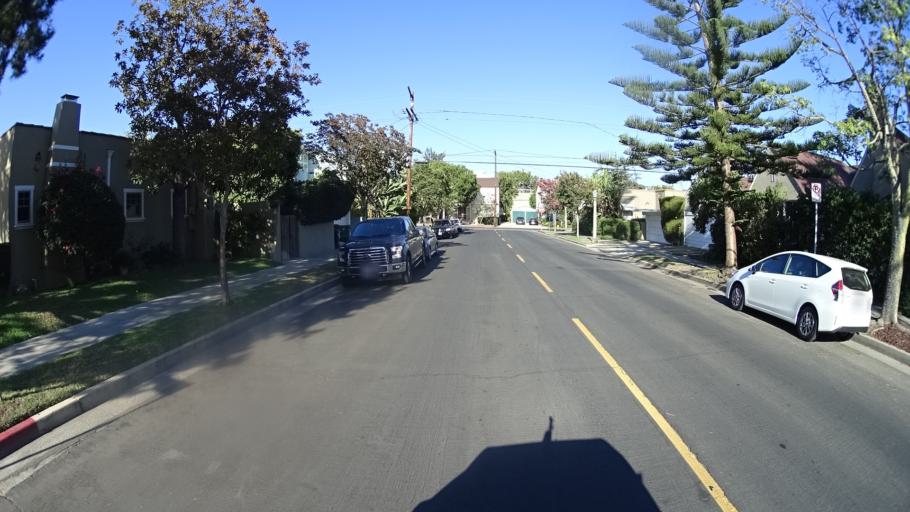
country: US
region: California
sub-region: Los Angeles County
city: Hollywood
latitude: 34.0789
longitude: -118.3186
